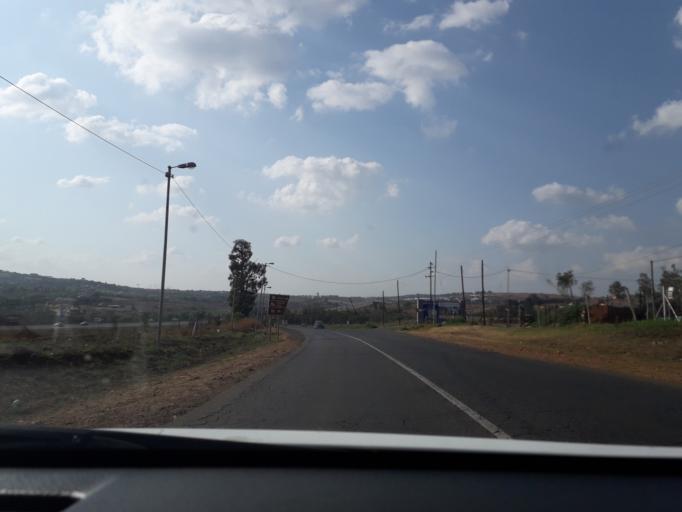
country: ZA
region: Gauteng
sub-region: City of Tshwane Metropolitan Municipality
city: Centurion
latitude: -25.8832
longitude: 28.2566
